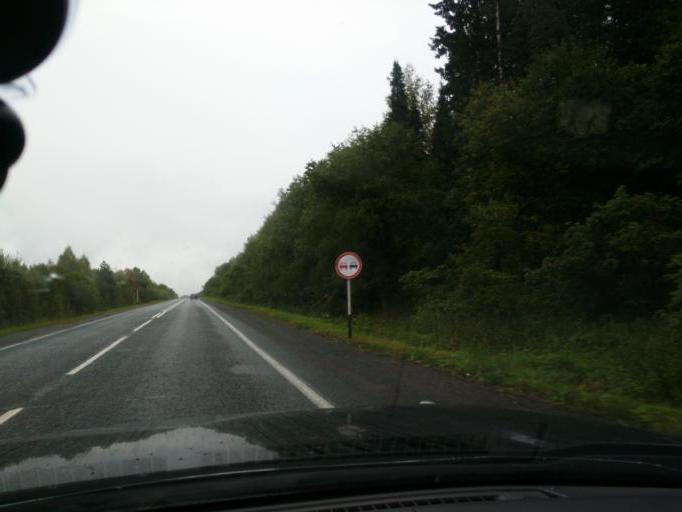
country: RU
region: Perm
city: Yugo-Kamskiy
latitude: 57.7569
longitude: 55.7313
